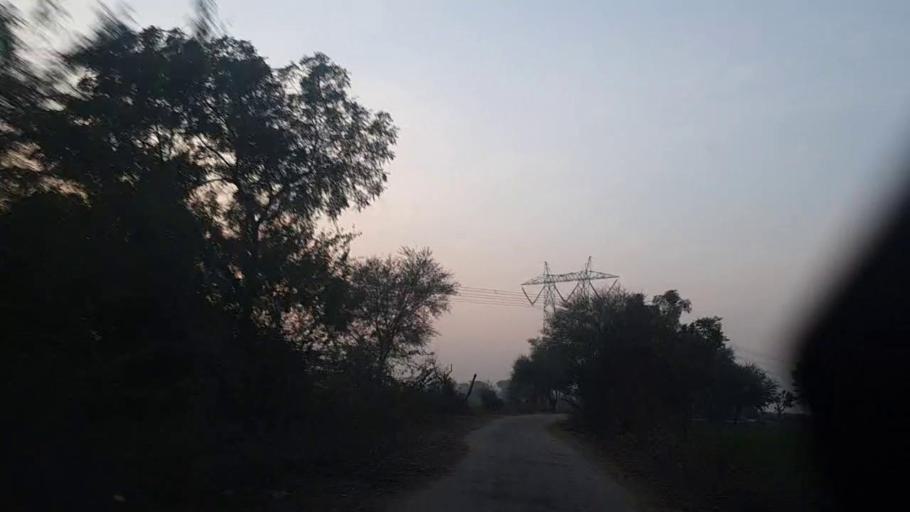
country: PK
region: Sindh
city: Sakrand
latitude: 26.0997
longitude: 68.3243
